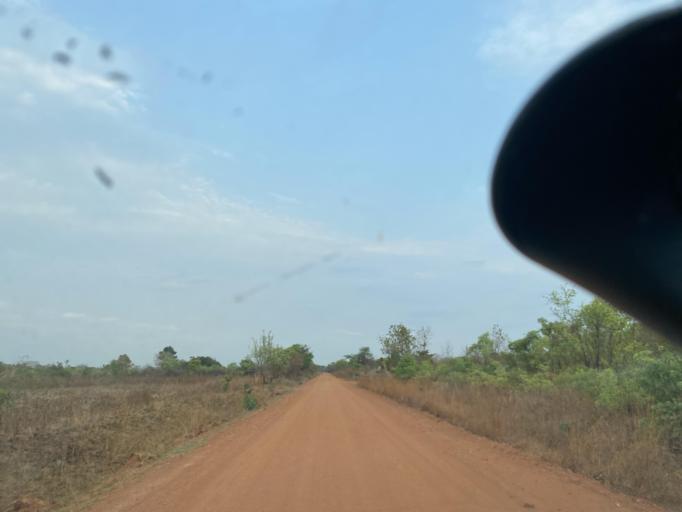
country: ZM
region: Lusaka
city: Chongwe
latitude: -15.2219
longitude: 28.5868
